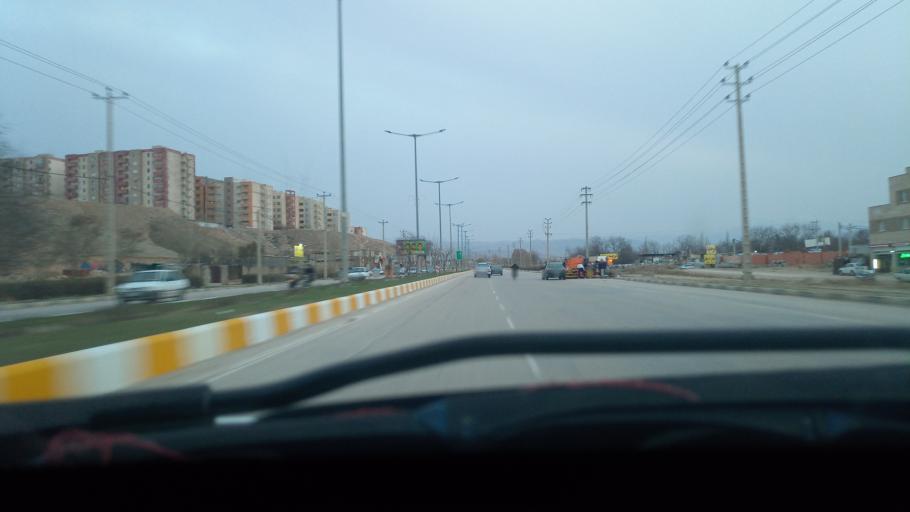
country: IR
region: Khorasan-e Shomali
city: Bojnurd
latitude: 37.4522
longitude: 57.3174
